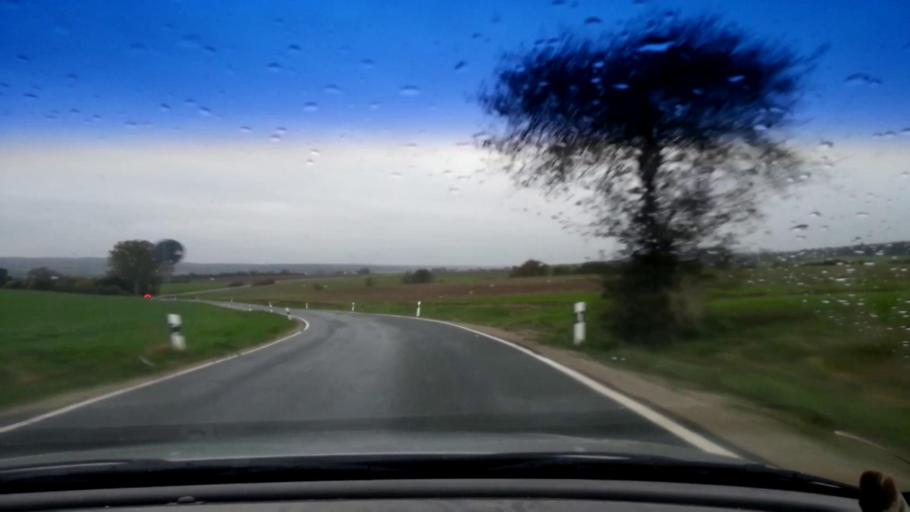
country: DE
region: Bavaria
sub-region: Upper Franconia
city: Priesendorf
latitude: 49.8606
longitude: 10.7167
